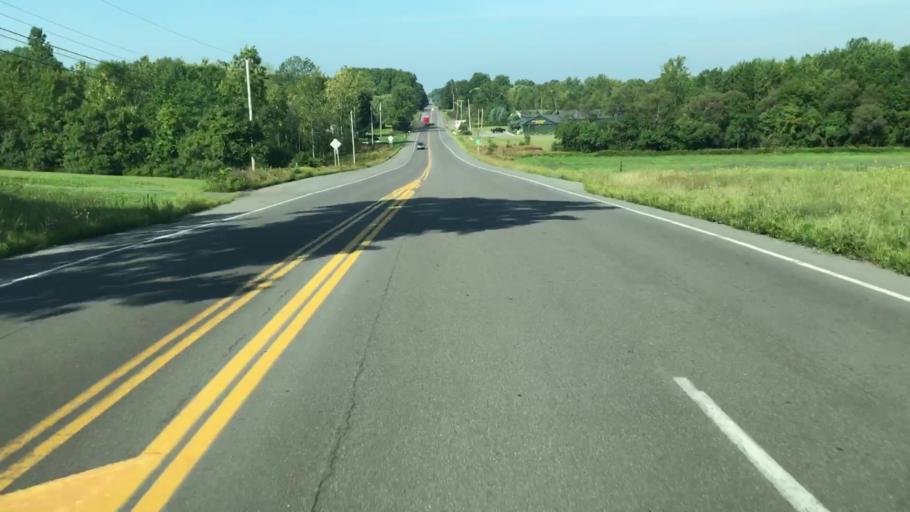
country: US
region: New York
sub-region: Onondaga County
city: Skaneateles
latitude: 42.9423
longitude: -76.4750
